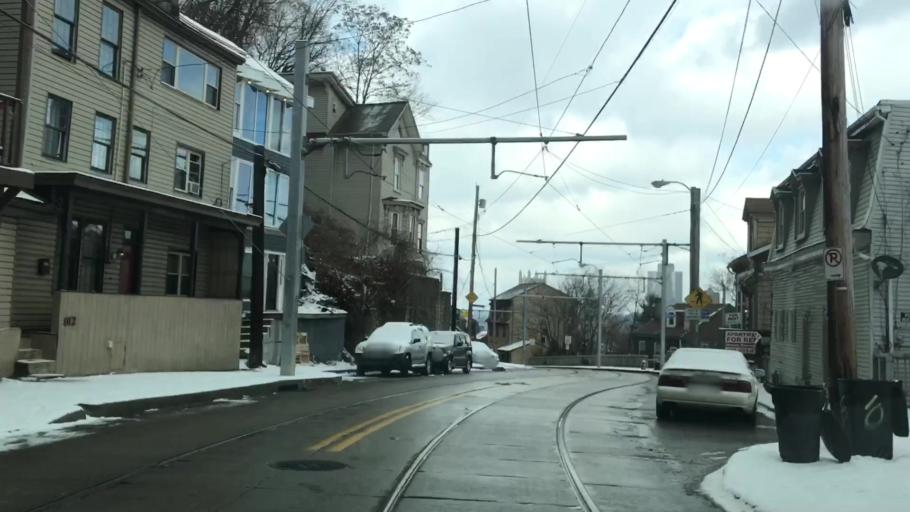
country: US
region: Pennsylvania
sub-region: Allegheny County
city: Mount Oliver
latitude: 40.4250
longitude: -79.9904
